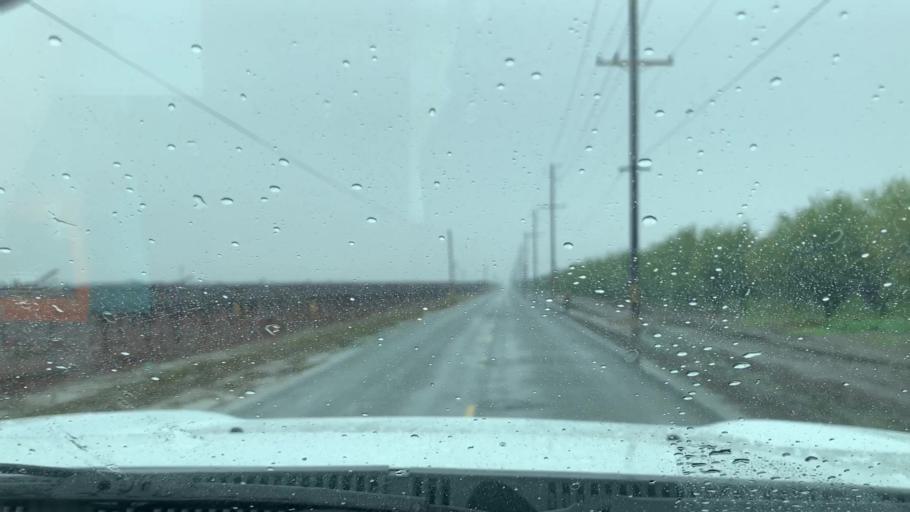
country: US
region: California
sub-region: Kern County
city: Delano
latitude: 35.8341
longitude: -119.1932
